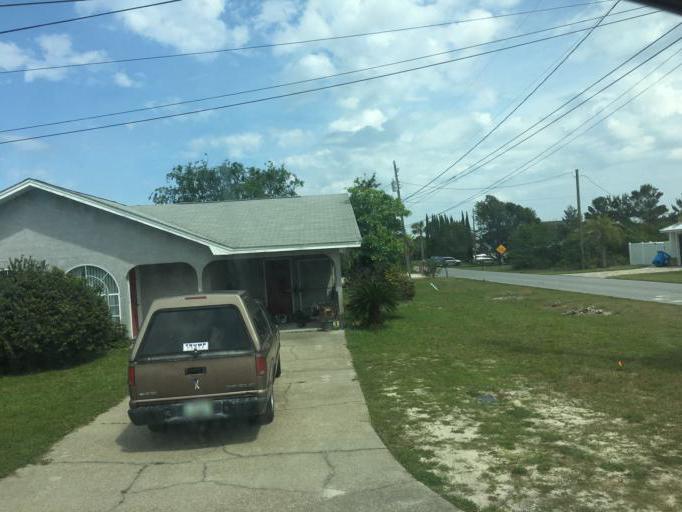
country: US
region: Florida
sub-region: Bay County
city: Laguna Beach
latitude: 30.2237
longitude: -85.8875
